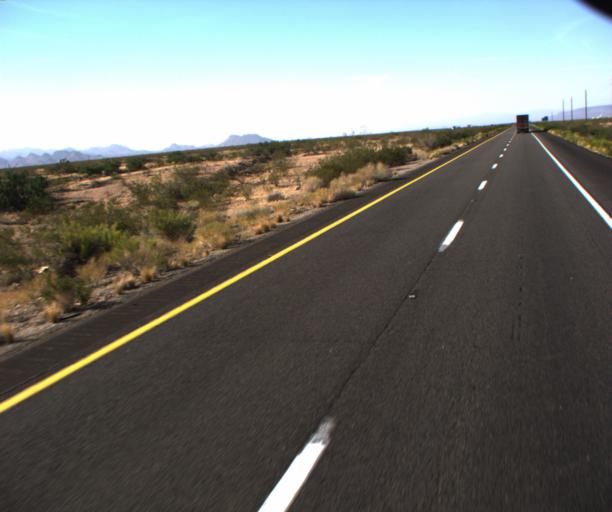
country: US
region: Arizona
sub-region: Mohave County
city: Kingman
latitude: 35.0564
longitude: -114.1265
